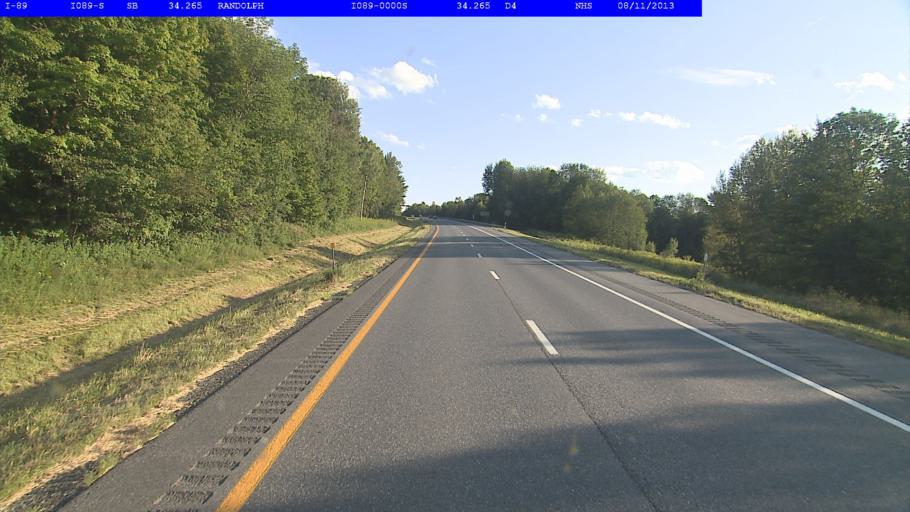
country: US
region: Vermont
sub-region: Orange County
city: Randolph
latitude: 43.9935
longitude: -72.6264
